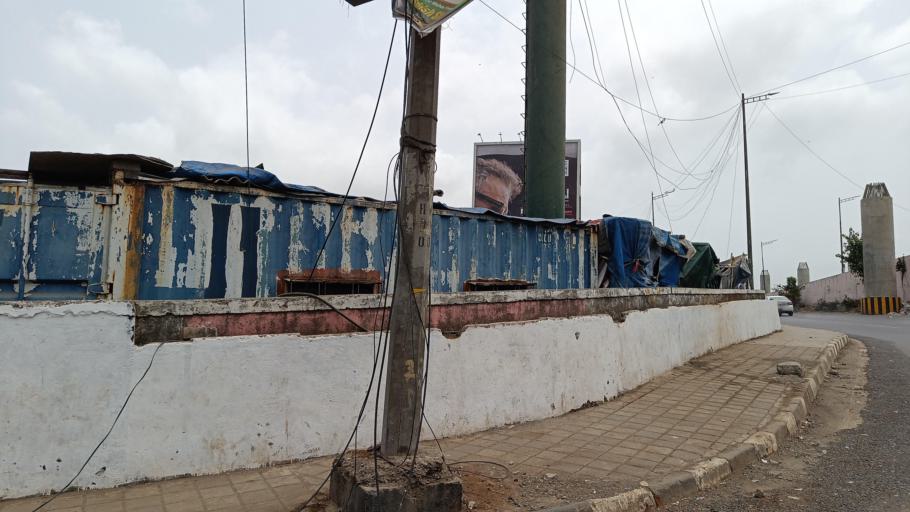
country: IN
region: Maharashtra
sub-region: Mumbai Suburban
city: Mumbai
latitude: 19.0505
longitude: 72.8386
